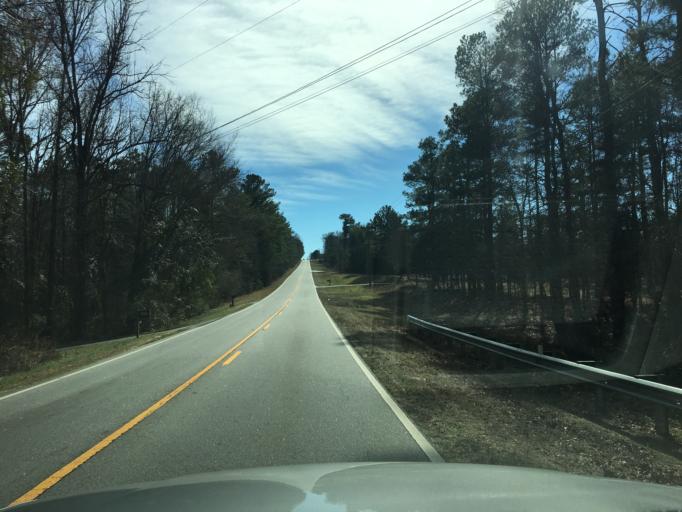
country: US
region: Georgia
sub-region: Rockdale County
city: Lakeview Estates
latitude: 33.6998
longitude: -84.0223
